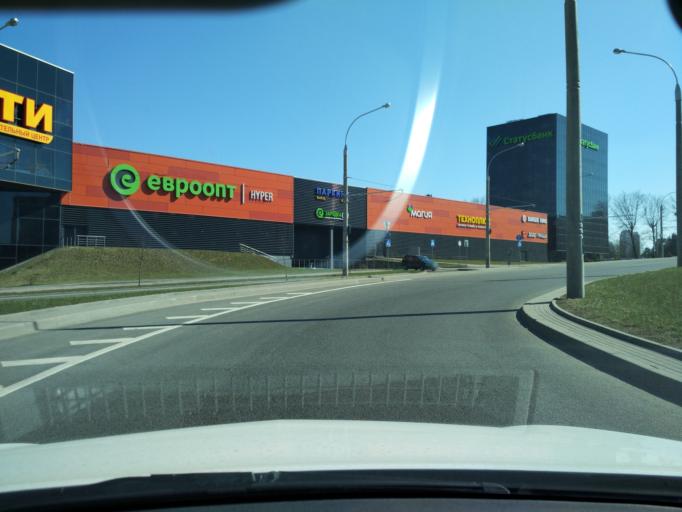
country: BY
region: Minsk
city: Minsk
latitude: 53.8723
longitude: 27.5714
